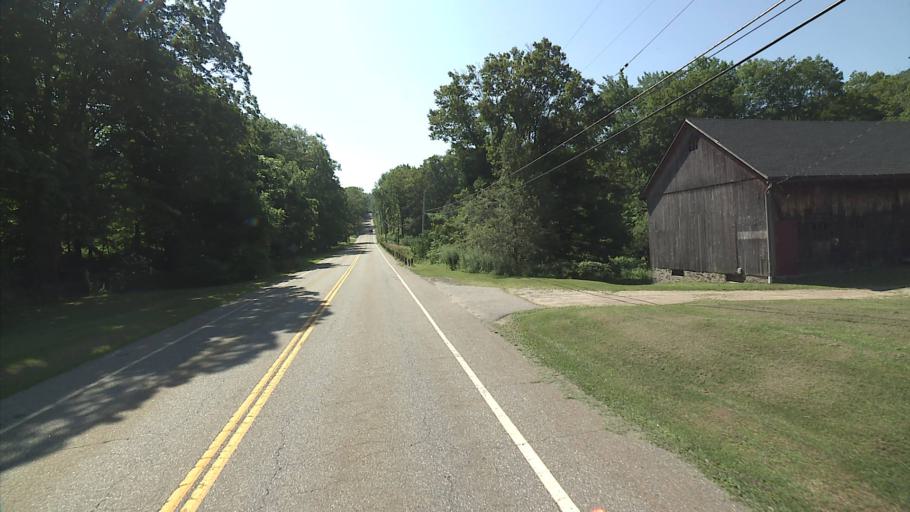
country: US
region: Connecticut
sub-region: Litchfield County
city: New Preston
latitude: 41.7968
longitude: -73.3696
